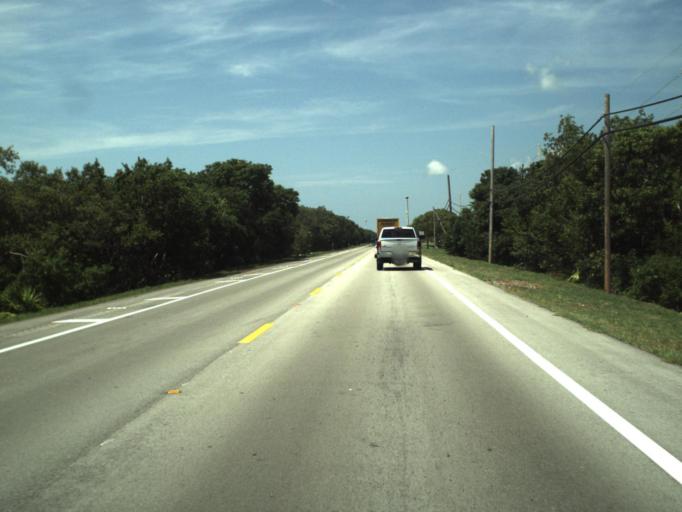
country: US
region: Florida
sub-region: Monroe County
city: Marathon
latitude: 24.7421
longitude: -80.9944
